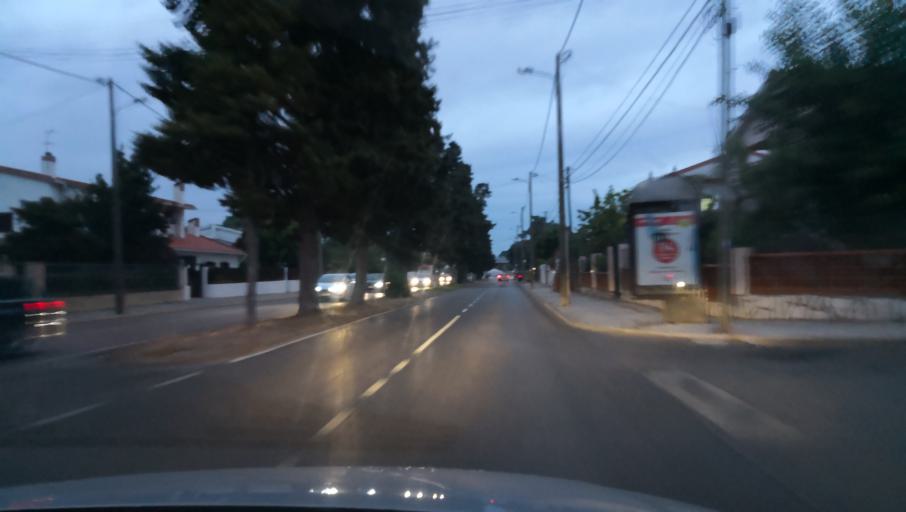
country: PT
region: Setubal
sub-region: Seixal
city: Amora
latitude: 38.6029
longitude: -9.1380
